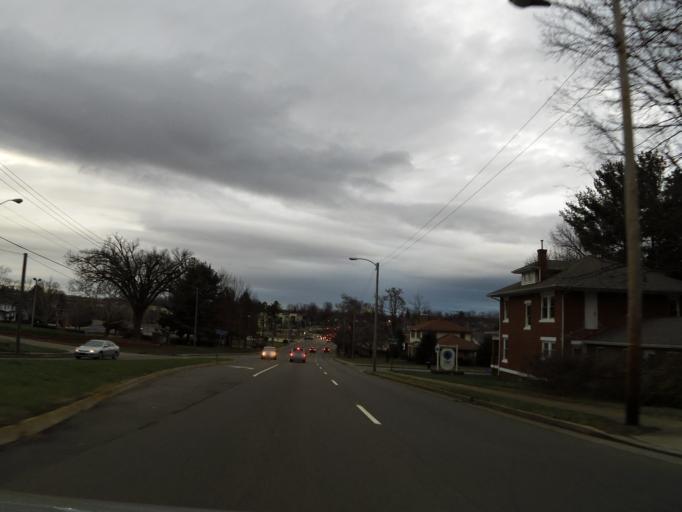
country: US
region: Tennessee
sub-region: Washington County
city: Johnson City
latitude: 36.3049
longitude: -82.3632
